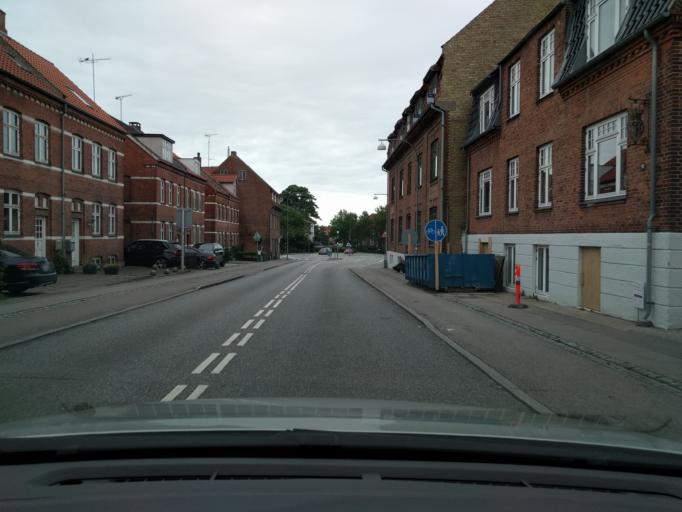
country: DK
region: Zealand
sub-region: Roskilde Kommune
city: Roskilde
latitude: 55.6394
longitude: 12.0733
